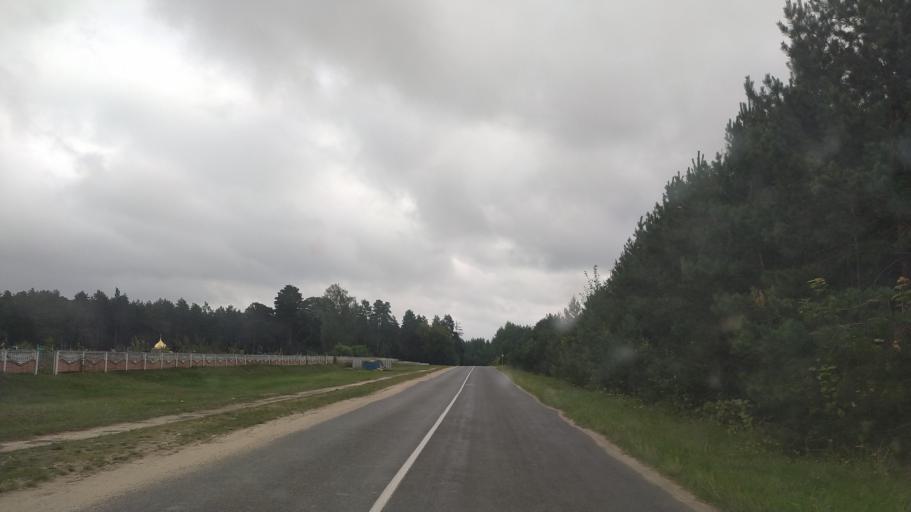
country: BY
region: Brest
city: Byaroza
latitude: 52.5978
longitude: 24.8740
